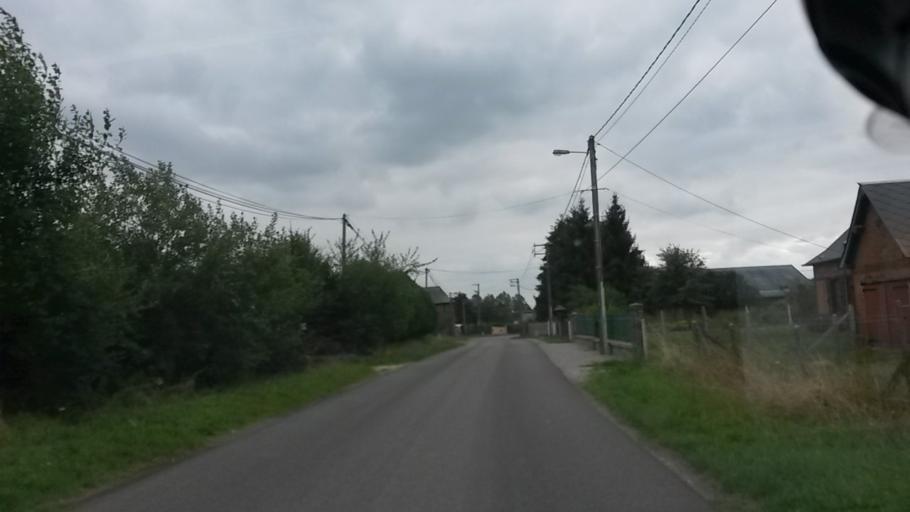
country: FR
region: Haute-Normandie
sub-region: Departement de la Seine-Maritime
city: La Feuillie
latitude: 49.4701
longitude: 1.5257
